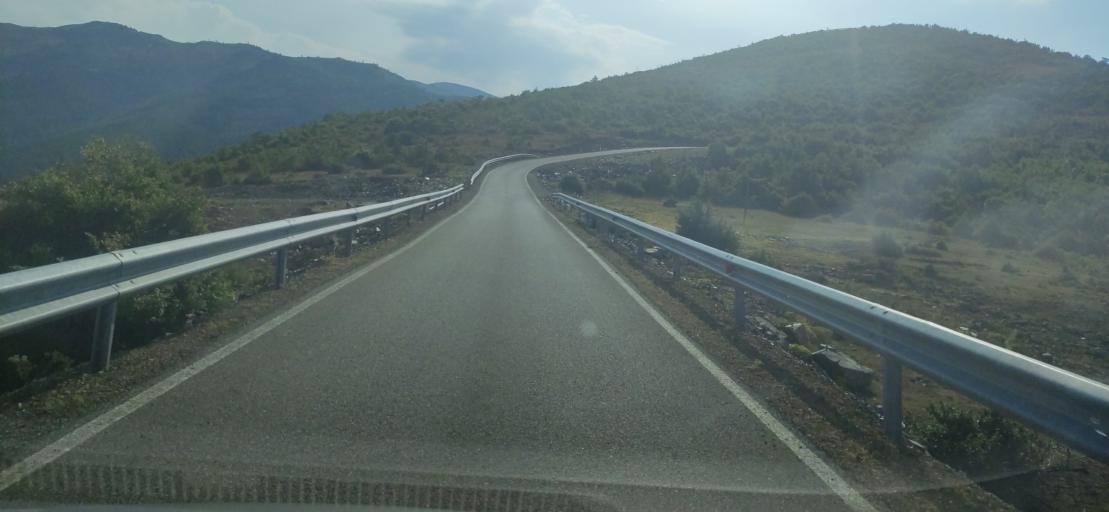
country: AL
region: Shkoder
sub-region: Rrethi i Pukes
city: Iballe
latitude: 42.1736
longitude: 19.9981
